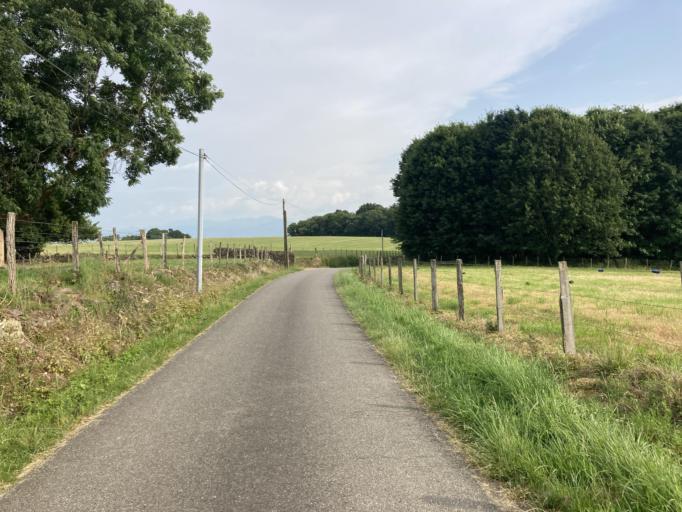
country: FR
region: Aquitaine
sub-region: Departement des Pyrenees-Atlantiques
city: Ledeuix
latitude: 43.2503
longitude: -0.6211
